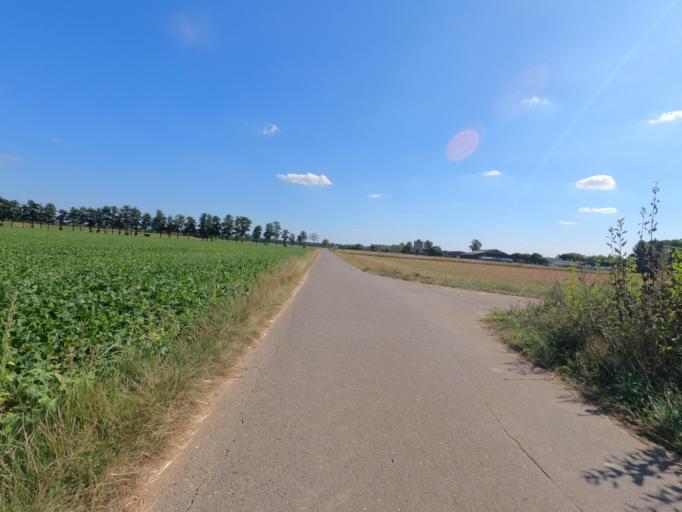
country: DE
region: North Rhine-Westphalia
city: Julich
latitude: 50.9356
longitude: 6.3250
